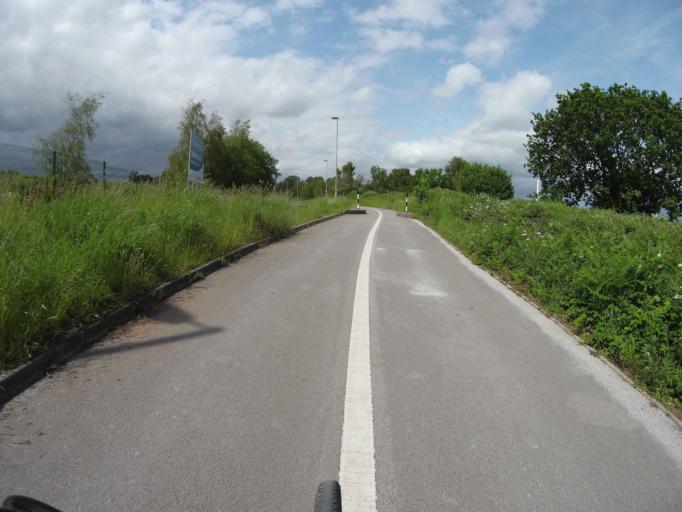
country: GB
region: England
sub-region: Devon
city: Topsham
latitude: 50.7084
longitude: -3.4735
